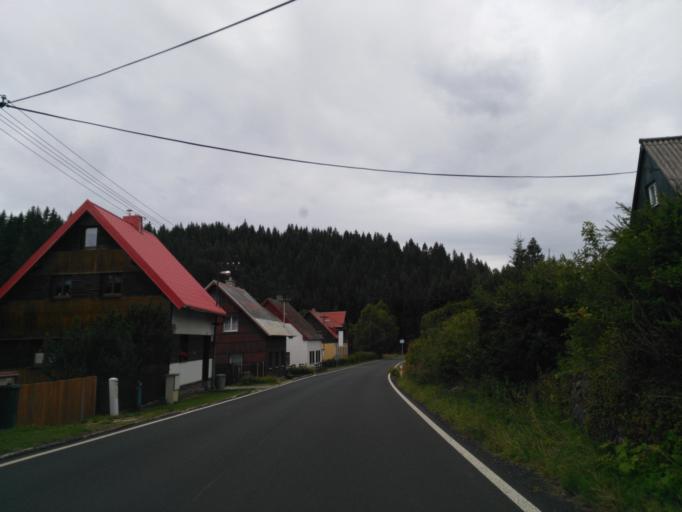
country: CZ
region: Karlovarsky
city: Abertamy
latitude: 50.3888
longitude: 12.7586
